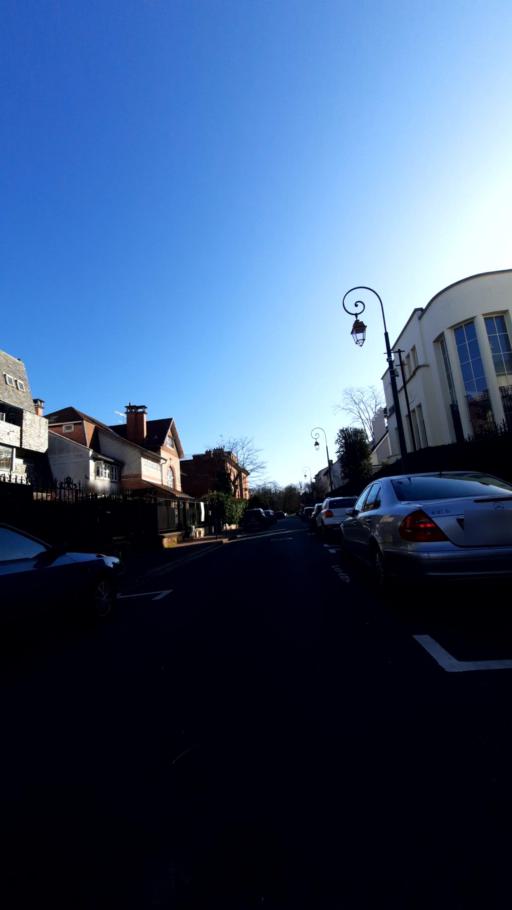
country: FR
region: Ile-de-France
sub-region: Departement du Val-de-Marne
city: Saint-Maurice
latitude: 48.8234
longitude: 2.4283
